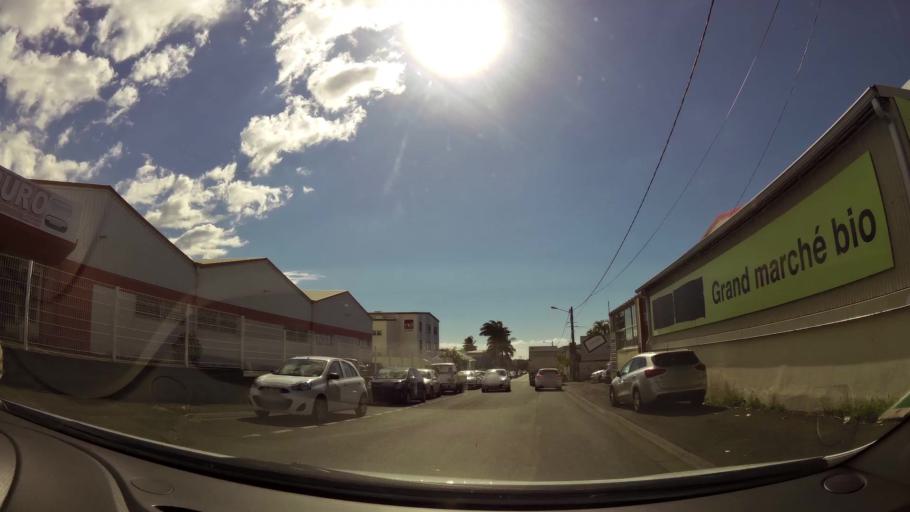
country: RE
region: Reunion
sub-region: Reunion
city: Saint-Denis
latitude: -20.8916
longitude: 55.4967
